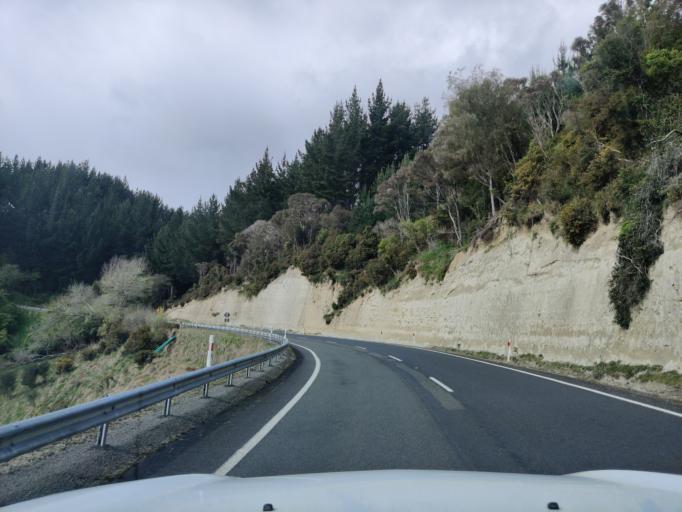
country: NZ
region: Manawatu-Wanganui
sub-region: Wanganui District
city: Wanganui
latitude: -39.7985
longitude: 175.1981
